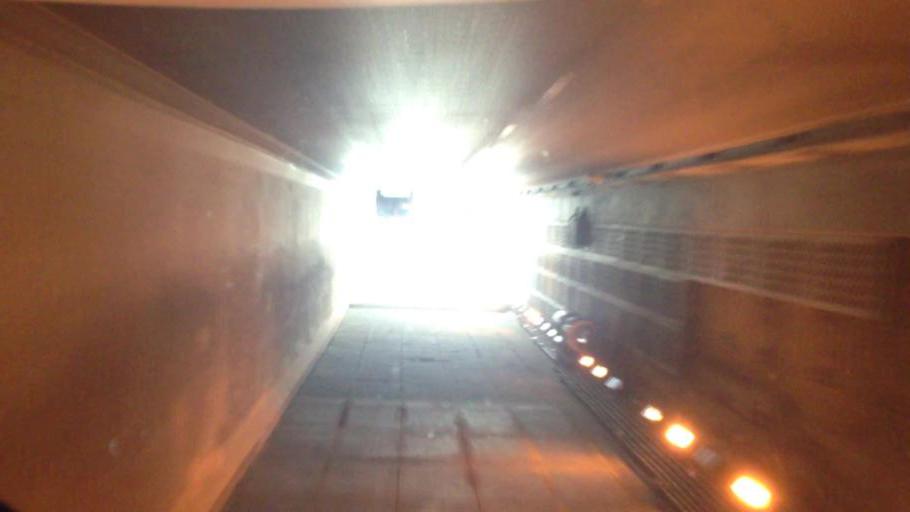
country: TH
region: Bangkok
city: Bang Na
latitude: 13.6782
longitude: 100.6461
